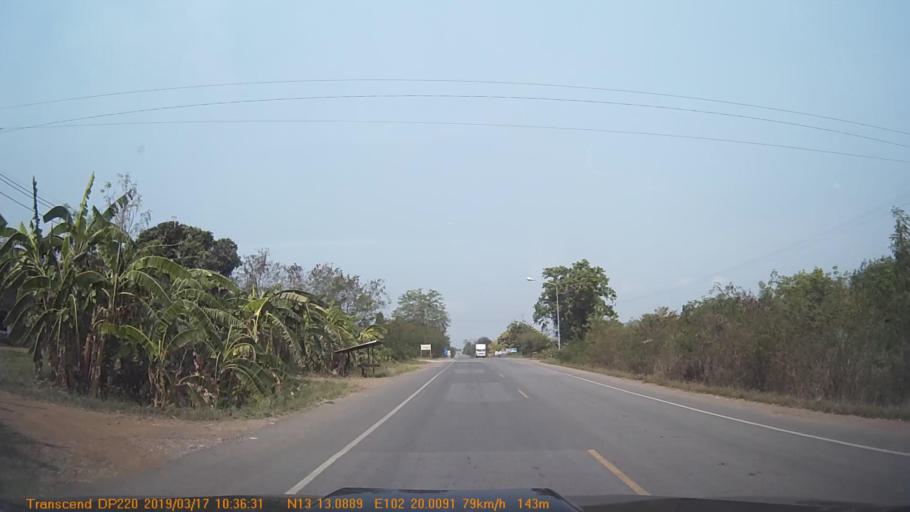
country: TH
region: Chanthaburi
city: Soi Dao
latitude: 13.2183
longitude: 102.3331
